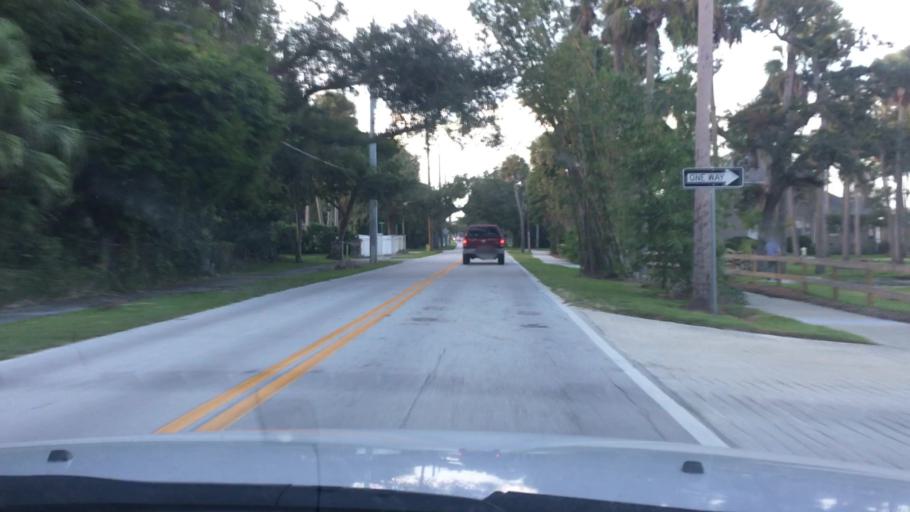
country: US
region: Florida
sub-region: Volusia County
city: Ormond Beach
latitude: 29.2806
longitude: -81.0533
